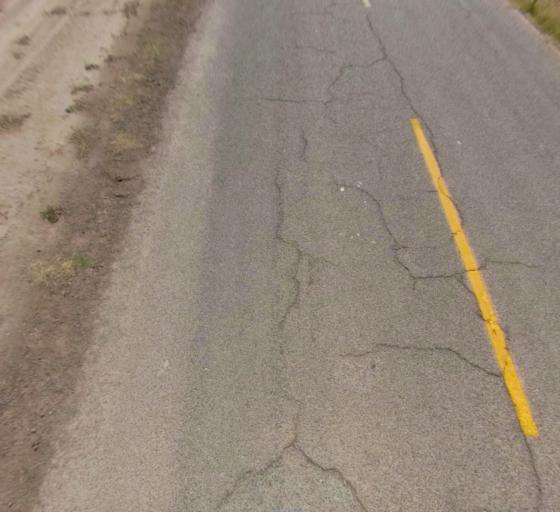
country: US
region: California
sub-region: Madera County
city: Parkwood
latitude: 36.8367
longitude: -120.1627
